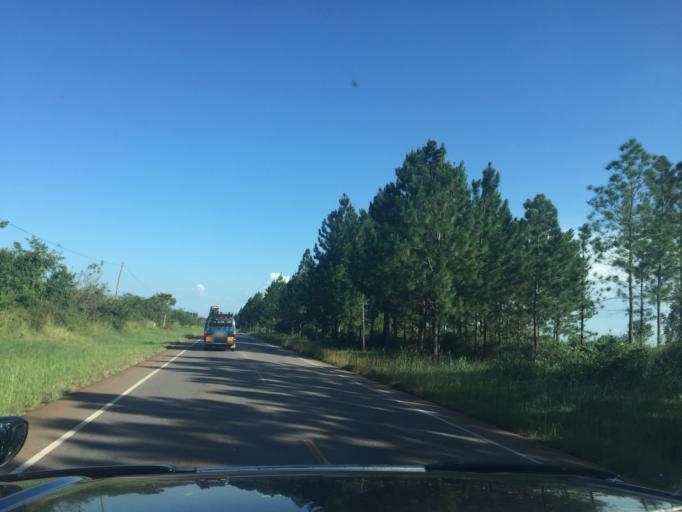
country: UG
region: Central Region
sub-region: Nakasongola District
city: Nakasongola
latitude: 1.3834
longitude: 32.3347
